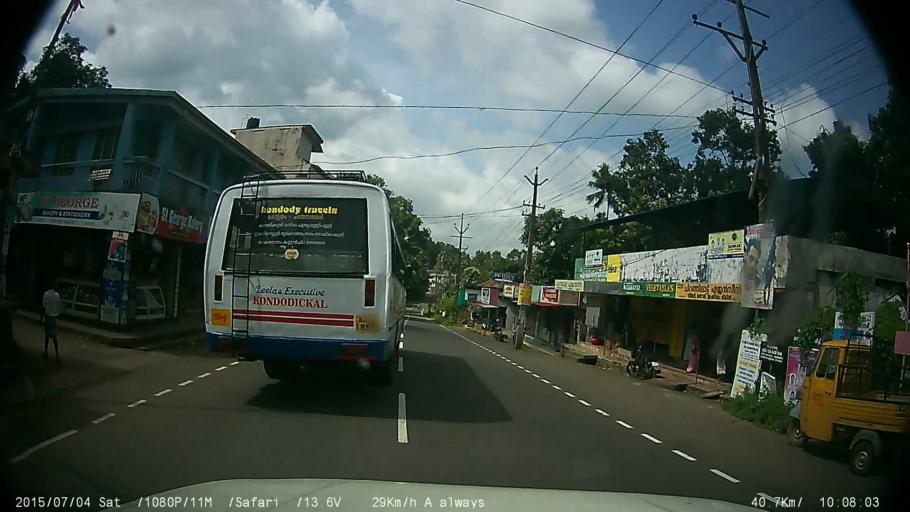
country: IN
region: Kerala
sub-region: Kottayam
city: Changanacheri
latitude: 9.4968
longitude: 76.5728
